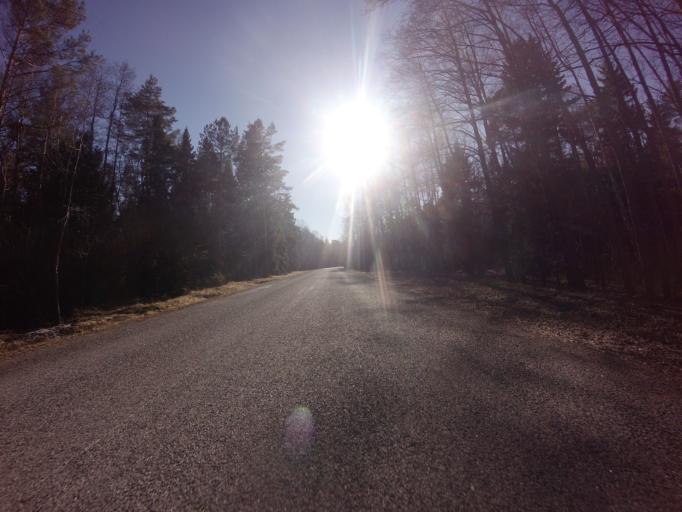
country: EE
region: Saare
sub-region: Kuressaare linn
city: Kuressaare
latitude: 58.4823
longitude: 22.2635
